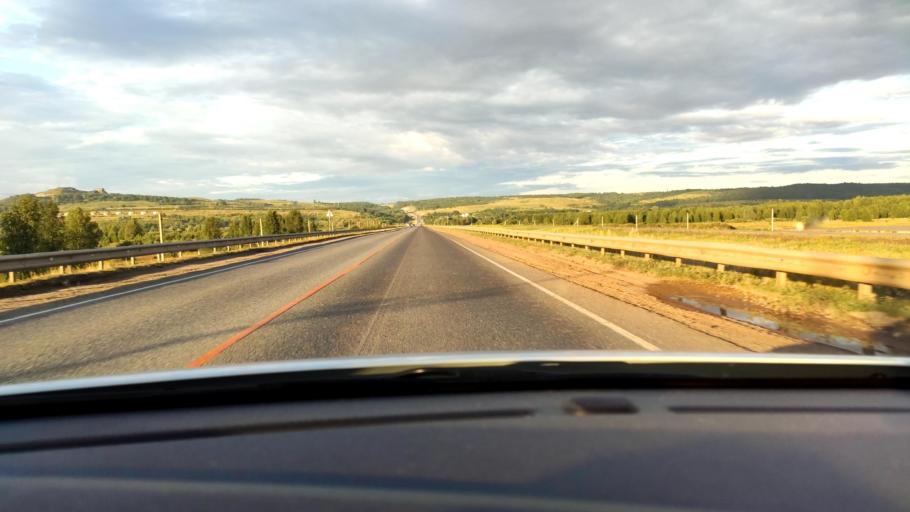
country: RU
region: Tatarstan
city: Sviyazhsk
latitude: 55.7105
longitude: 48.6860
